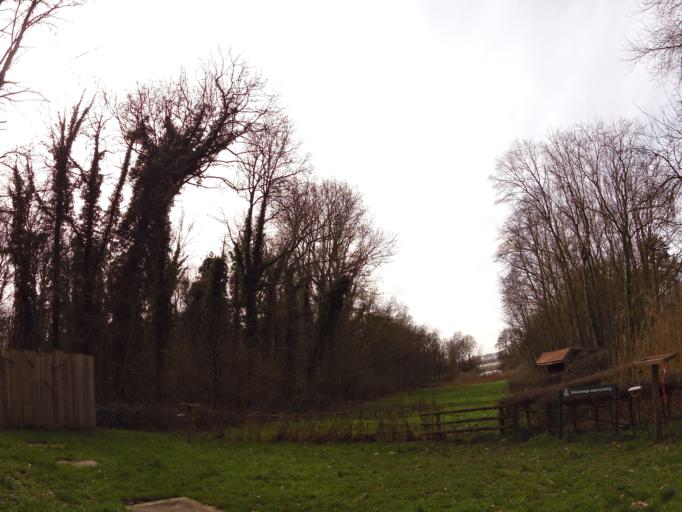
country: BE
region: Flanders
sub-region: Provincie West-Vlaanderen
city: Diksmuide
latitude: 50.9840
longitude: 2.8711
